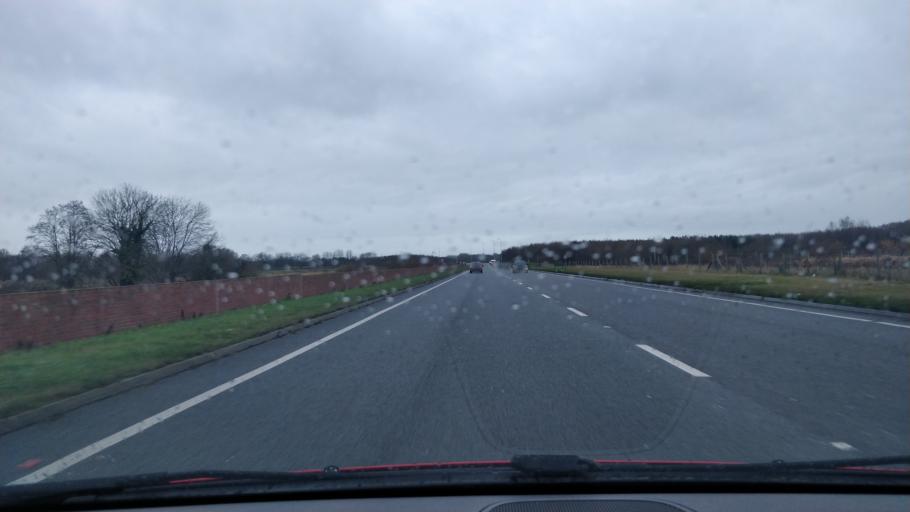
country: GB
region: England
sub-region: Sefton
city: Thornton
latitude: 53.5018
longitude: -2.9892
